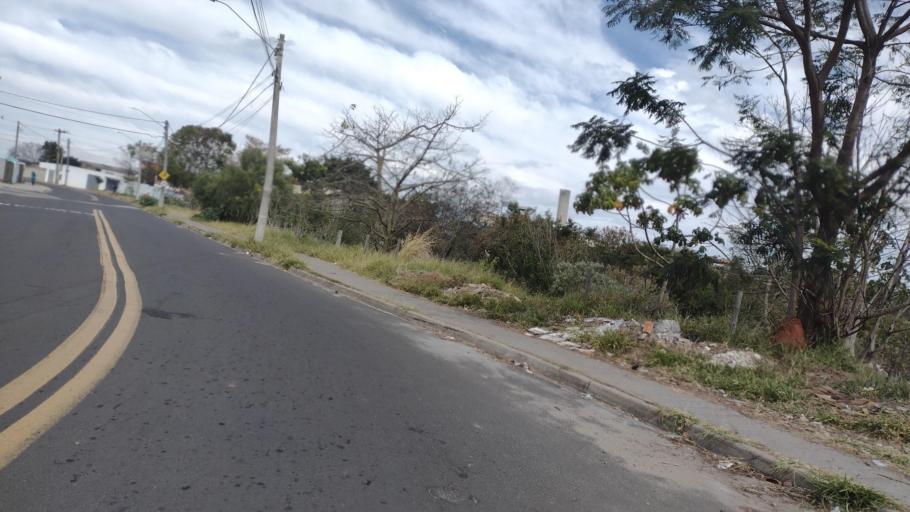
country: BR
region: Sao Paulo
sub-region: Sorocaba
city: Sorocaba
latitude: -23.4271
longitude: -47.4607
